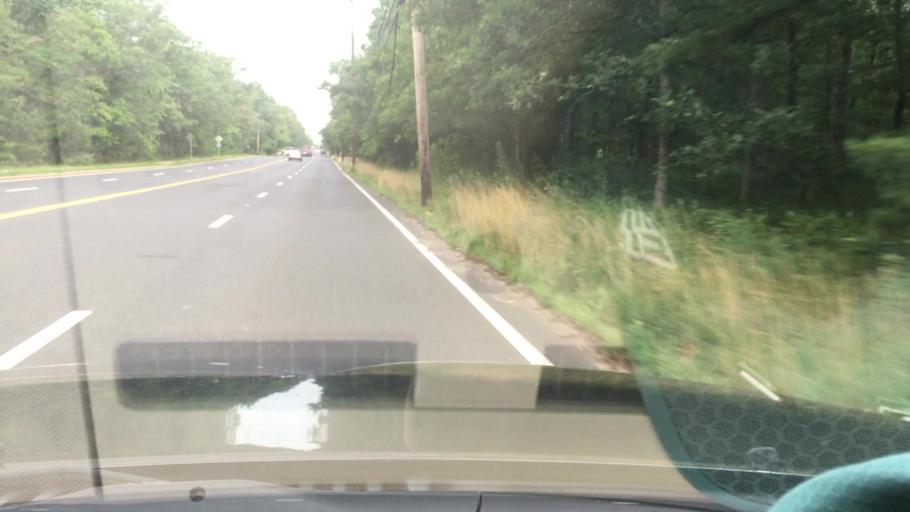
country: US
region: New Jersey
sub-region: Ocean County
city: Pine Lake Park
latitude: 40.0150
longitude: -74.2549
